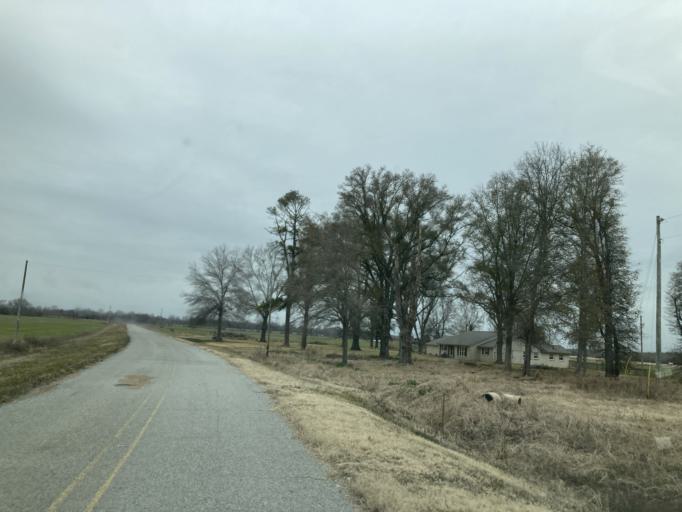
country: US
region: Mississippi
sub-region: Yazoo County
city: Yazoo City
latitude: 33.0111
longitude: -90.4708
